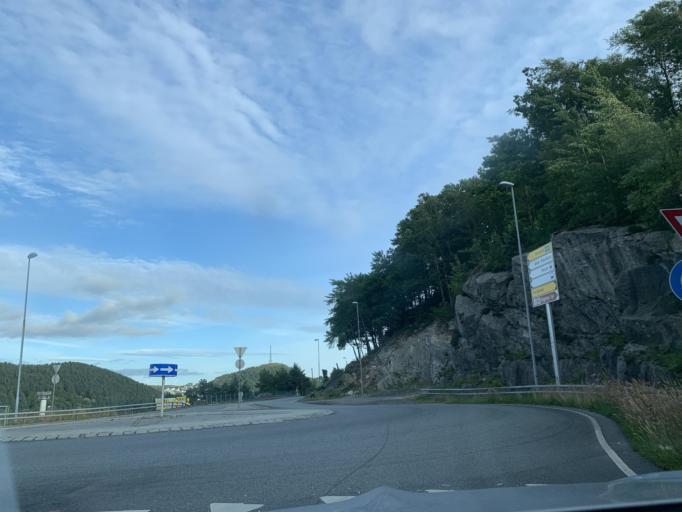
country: NO
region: Rogaland
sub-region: Eigersund
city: Egersund
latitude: 58.4606
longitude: 5.9752
